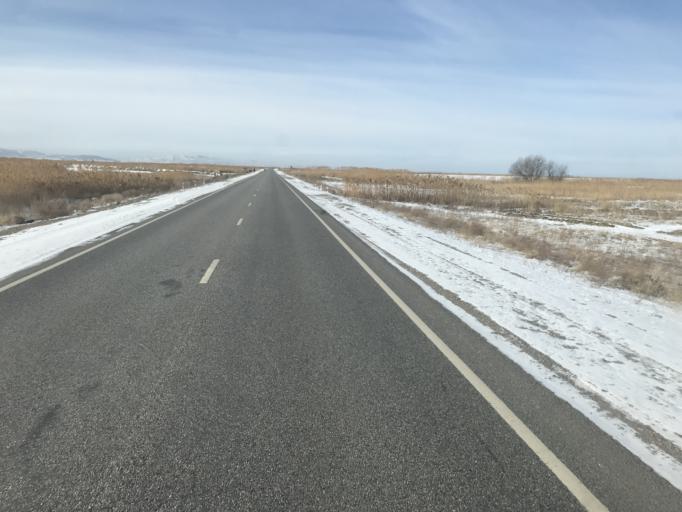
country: KZ
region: Zhambyl
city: Sarykemer
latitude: 43.0400
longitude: 71.4169
